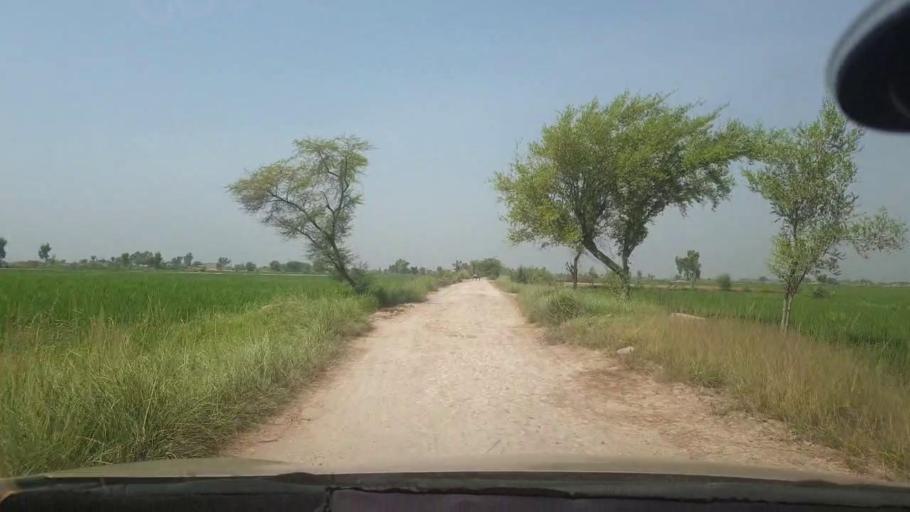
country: PK
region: Sindh
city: Shahdadkot
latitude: 27.7569
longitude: 67.9430
